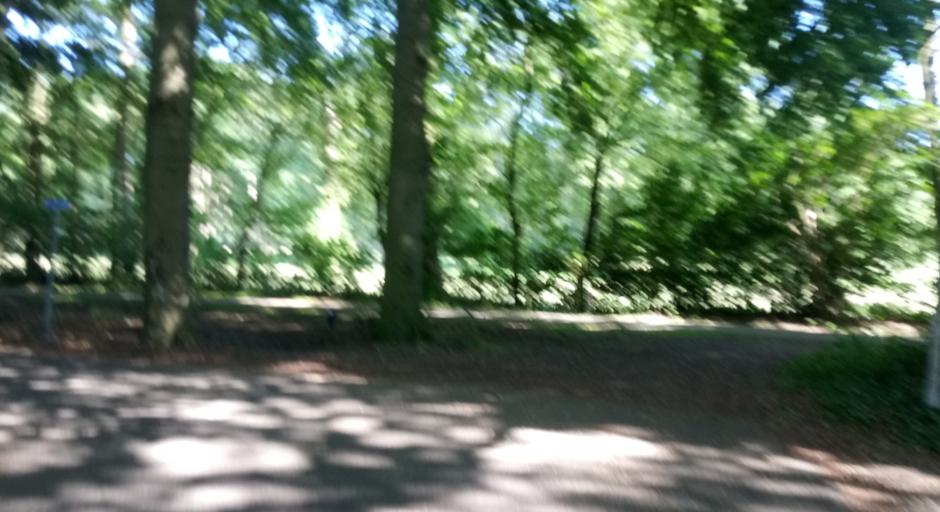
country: NL
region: Gelderland
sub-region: Gemeente Voorst
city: Twello
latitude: 52.1992
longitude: 6.1133
